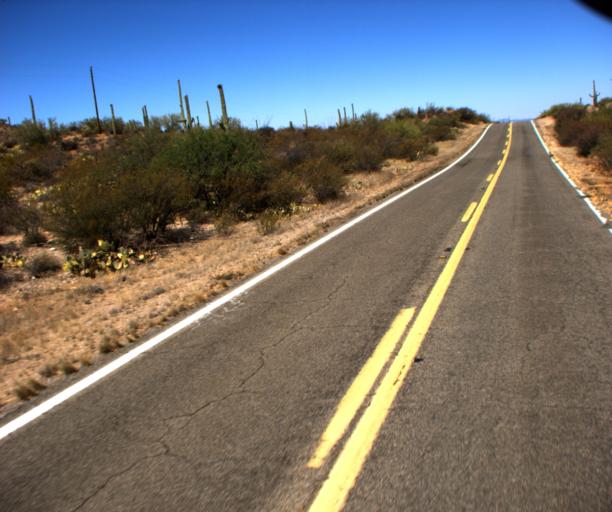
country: US
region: Arizona
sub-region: Pima County
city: Sells
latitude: 32.1752
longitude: -112.1841
